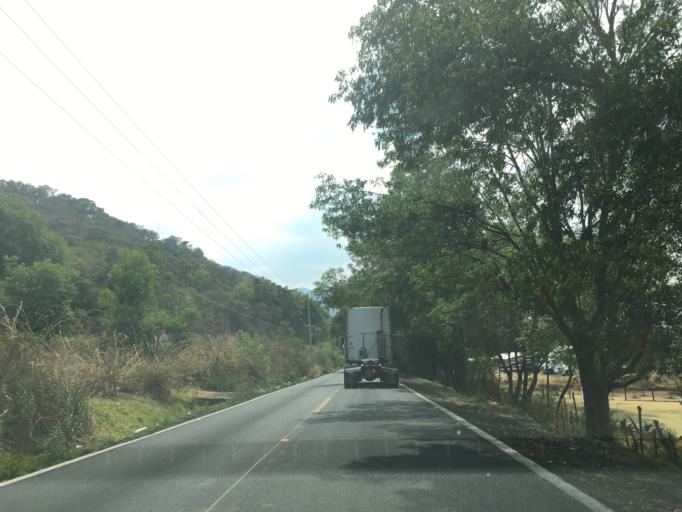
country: MX
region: Michoacan
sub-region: Morelia
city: La Mintzita (Piedra Dura)
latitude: 19.6398
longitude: -101.2697
